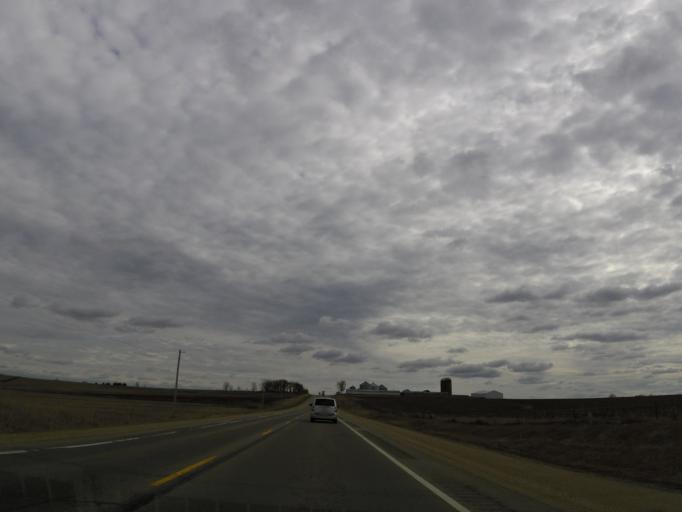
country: US
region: Iowa
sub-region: Chickasaw County
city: New Hampton
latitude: 43.1825
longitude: -92.2986
